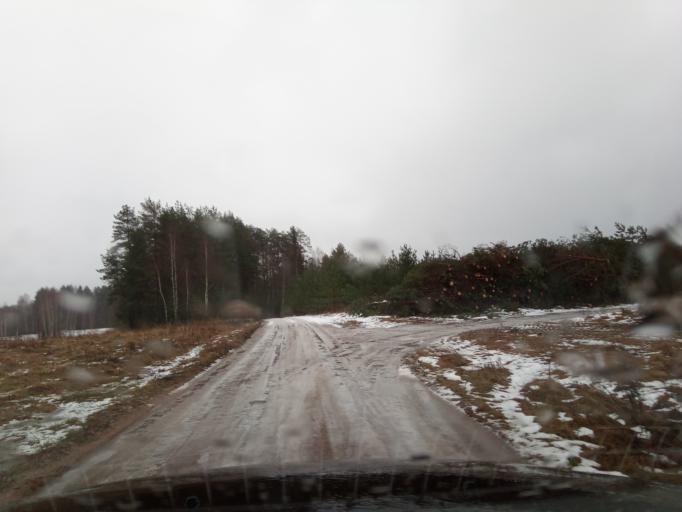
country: LT
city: Svencioneliai
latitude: 55.3418
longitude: 25.8450
